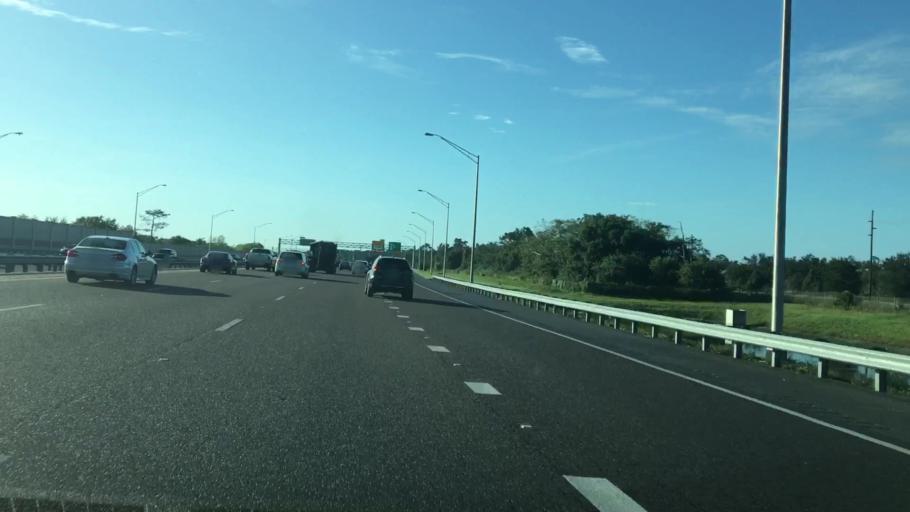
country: US
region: Florida
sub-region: Orange County
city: Azalea Park
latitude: 28.4977
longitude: -81.2435
